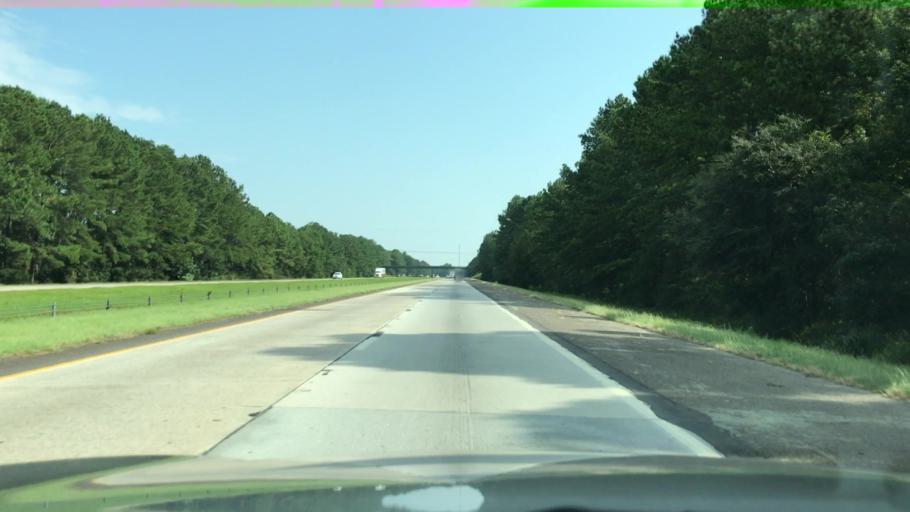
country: US
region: South Carolina
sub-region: Hampton County
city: Yemassee
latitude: 32.7788
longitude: -80.7930
